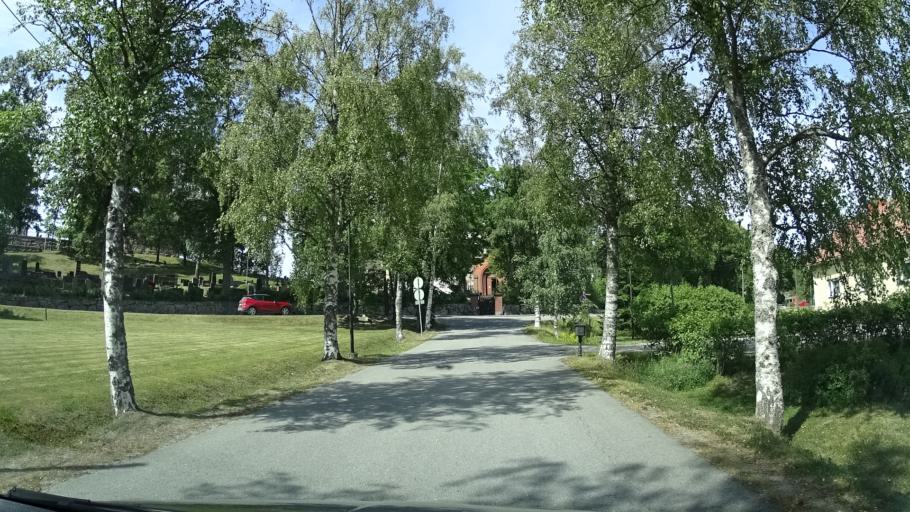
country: FI
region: Varsinais-Suomi
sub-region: Salo
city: Halikko
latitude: 60.3988
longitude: 23.0733
